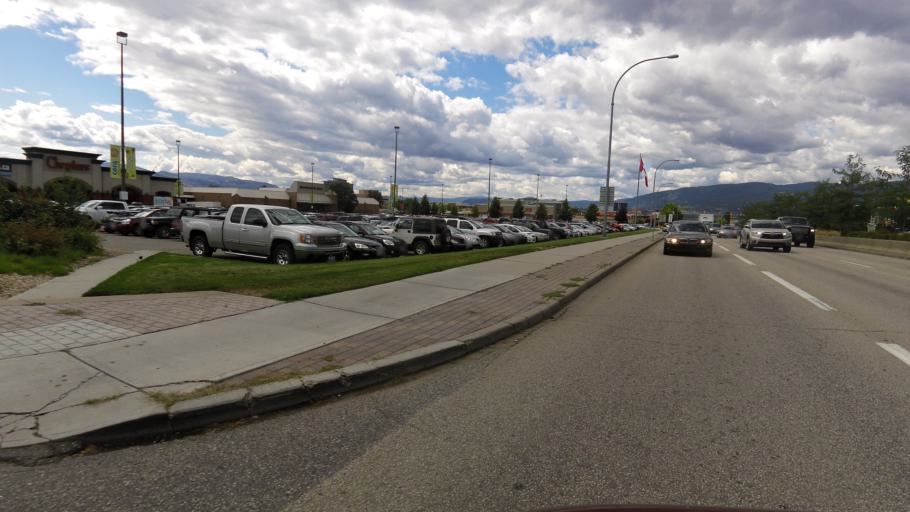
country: CA
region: British Columbia
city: Kelowna
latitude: 49.8817
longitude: -119.4400
